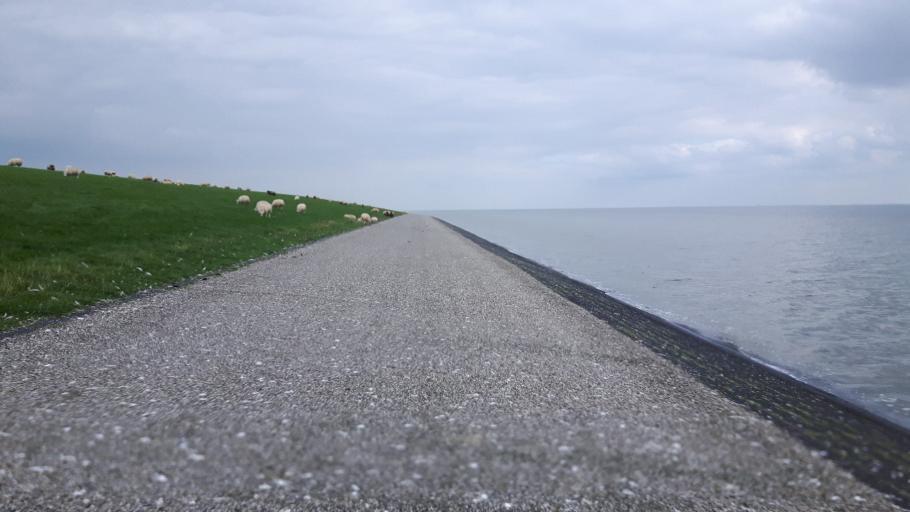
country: NL
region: Friesland
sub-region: Gemeente Ameland
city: Nes
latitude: 53.4436
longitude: 5.8390
